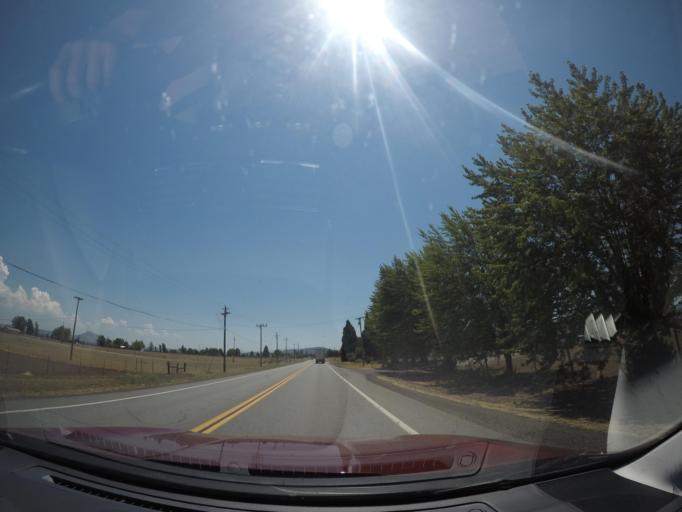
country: US
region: California
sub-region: Shasta County
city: Burney
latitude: 41.0326
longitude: -121.4176
